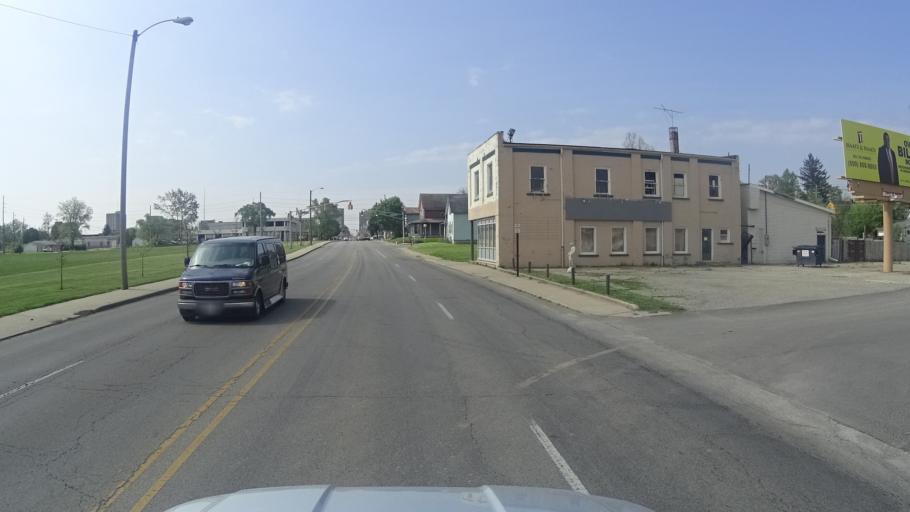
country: US
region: Indiana
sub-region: Madison County
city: Anderson
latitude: 40.1138
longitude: -85.6806
